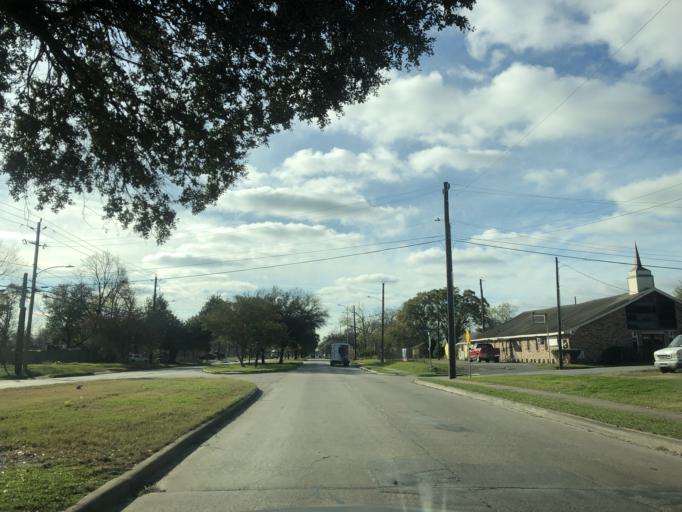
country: US
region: Texas
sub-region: Harris County
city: Jacinto City
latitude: 29.8150
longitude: -95.2846
